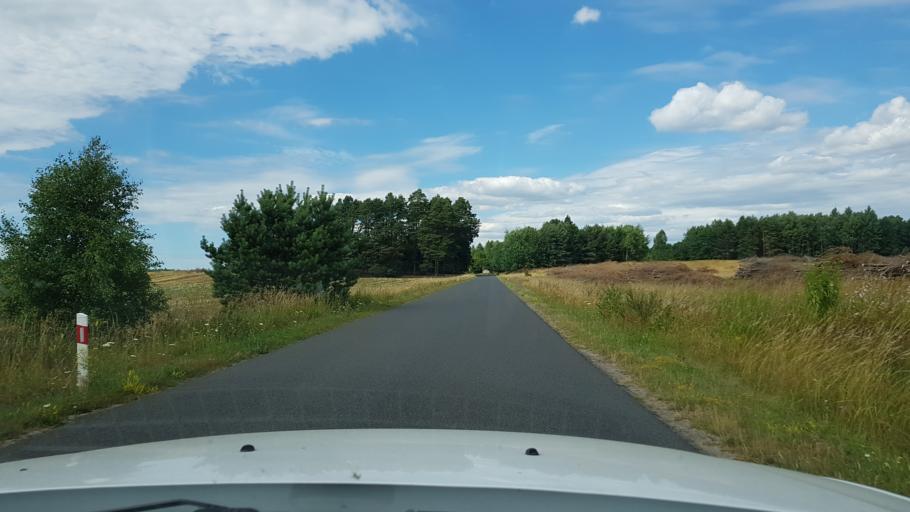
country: PL
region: West Pomeranian Voivodeship
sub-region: Powiat drawski
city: Kalisz Pomorski
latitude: 53.3640
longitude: 15.9348
